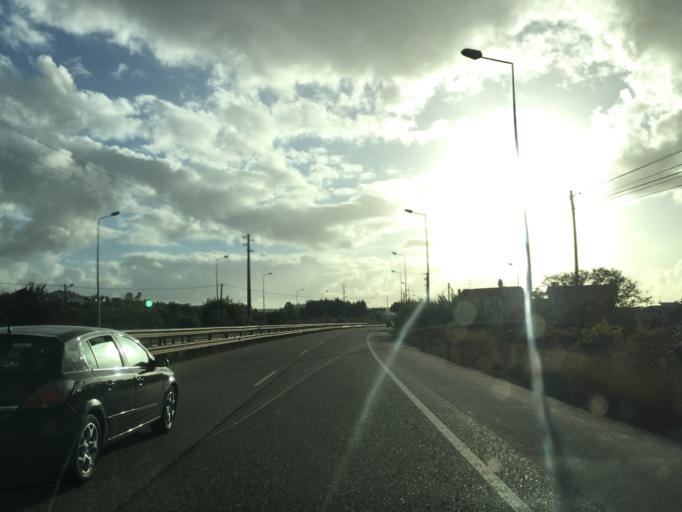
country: PT
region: Coimbra
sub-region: Coimbra
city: Coimbra
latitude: 40.2108
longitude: -8.4644
